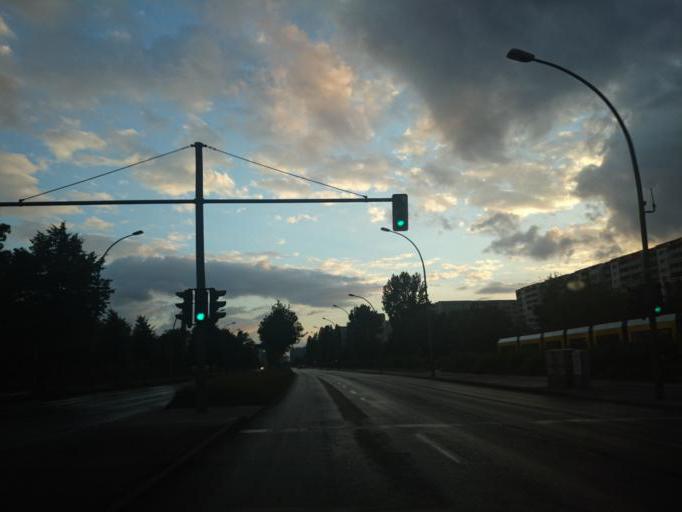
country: DE
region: Berlin
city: Alt-Hohenschoenhausen
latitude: 52.5342
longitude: 13.4961
